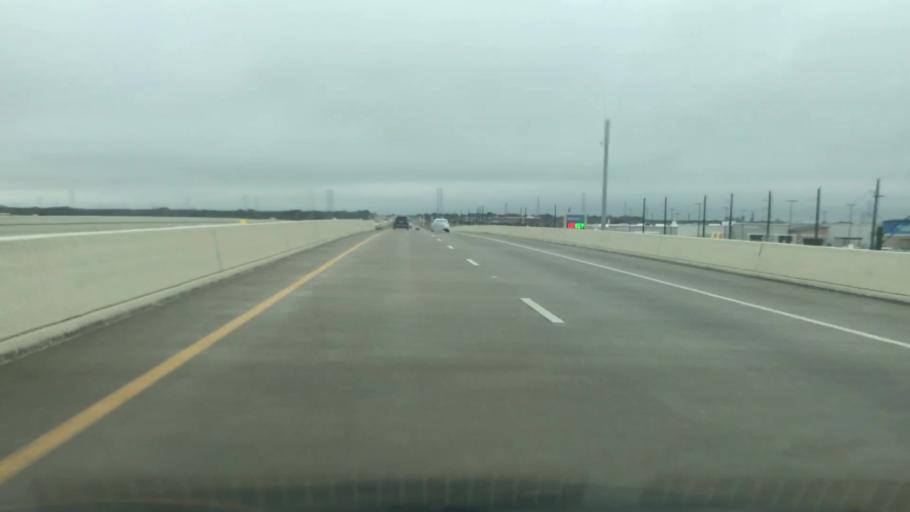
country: US
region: Texas
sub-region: Harris County
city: Katy
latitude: 29.8172
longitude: -95.7709
